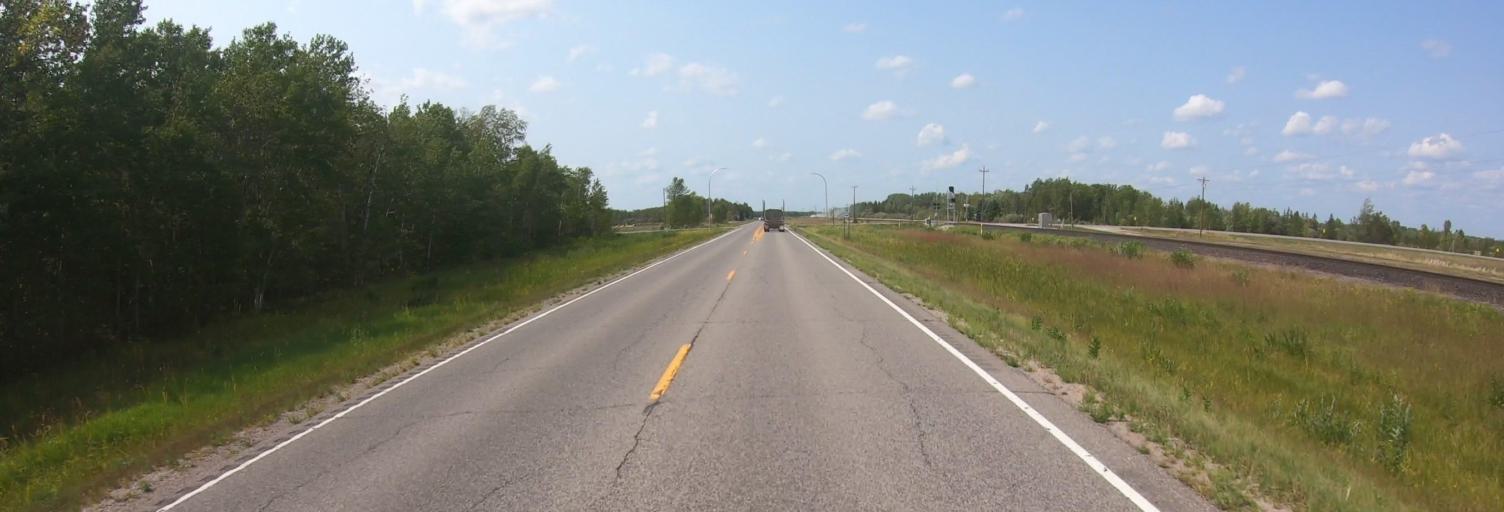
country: US
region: Minnesota
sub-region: Roseau County
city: Warroad
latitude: 48.8699
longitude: -95.2628
